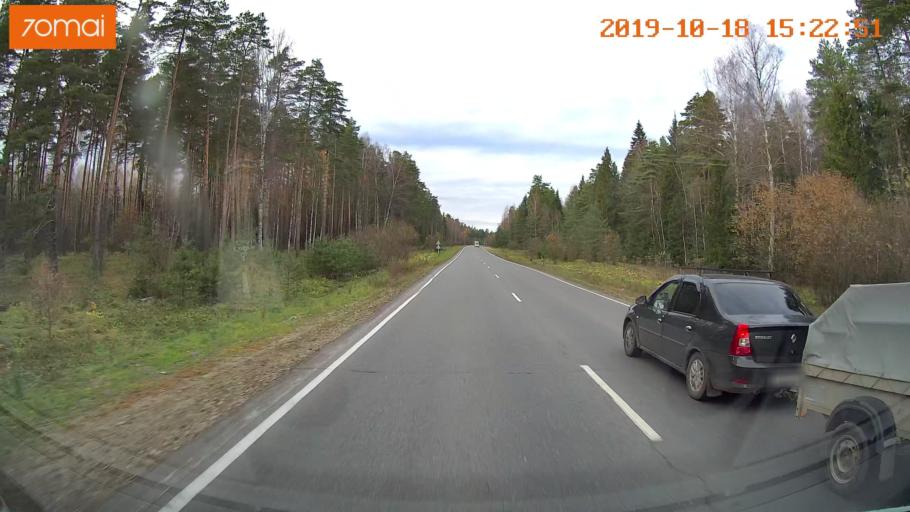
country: RU
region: Vladimir
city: Anopino
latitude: 55.7123
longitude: 40.7278
